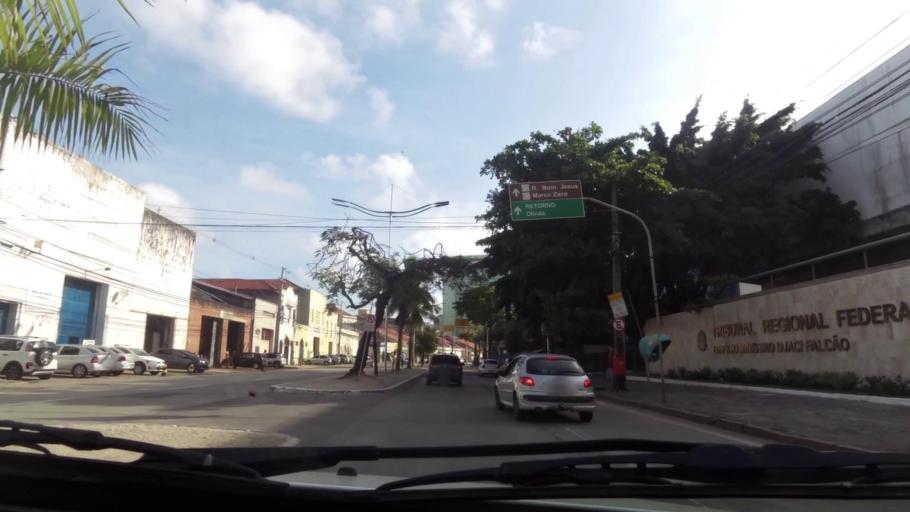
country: BR
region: Pernambuco
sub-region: Recife
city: Recife
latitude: -8.0612
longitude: -34.8733
